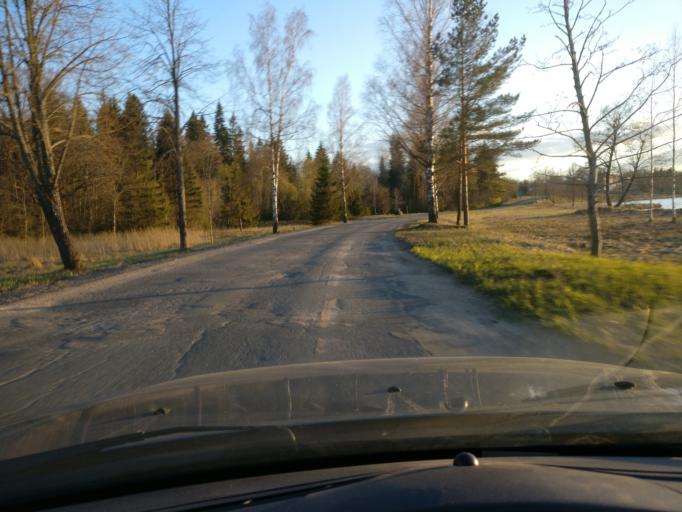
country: LV
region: Aluksnes Rajons
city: Aluksne
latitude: 57.4257
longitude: 27.0852
